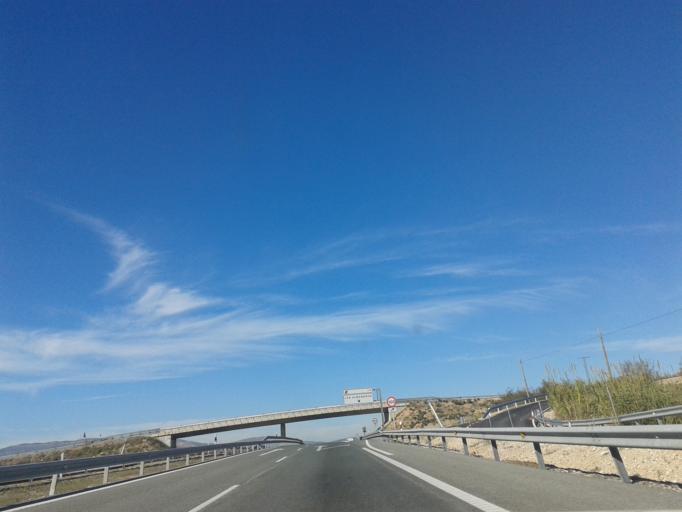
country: ES
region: Castille-La Mancha
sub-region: Provincia de Albacete
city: Caudete
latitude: 38.6947
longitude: -0.9140
